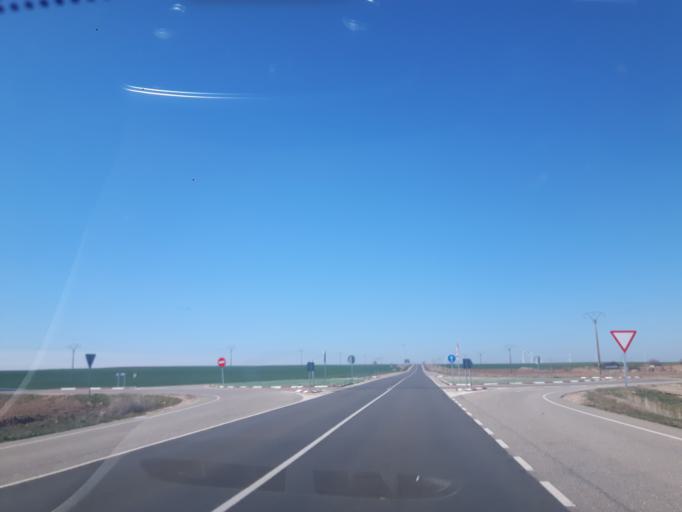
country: ES
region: Castille and Leon
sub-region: Provincia de Salamanca
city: Coca de Alba
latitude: 40.8718
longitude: -5.3767
